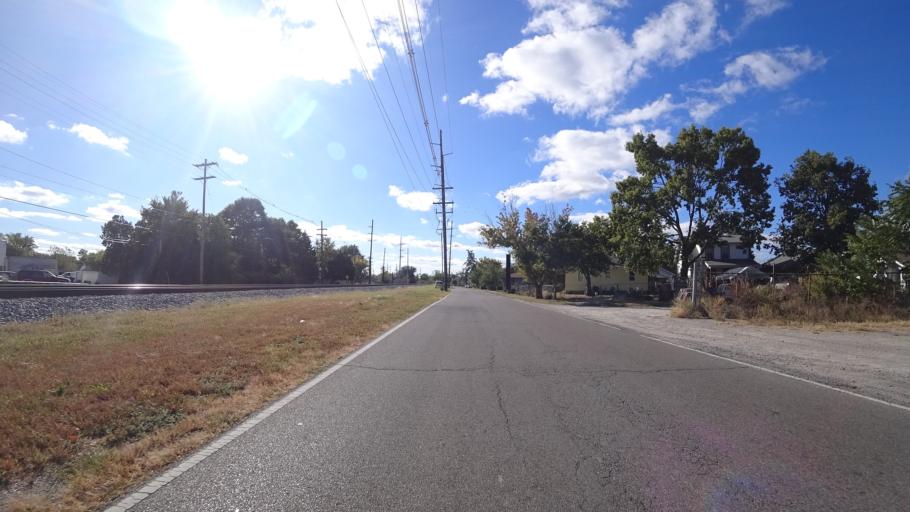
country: US
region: Ohio
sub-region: Butler County
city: Fairfield
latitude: 39.3681
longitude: -84.5497
